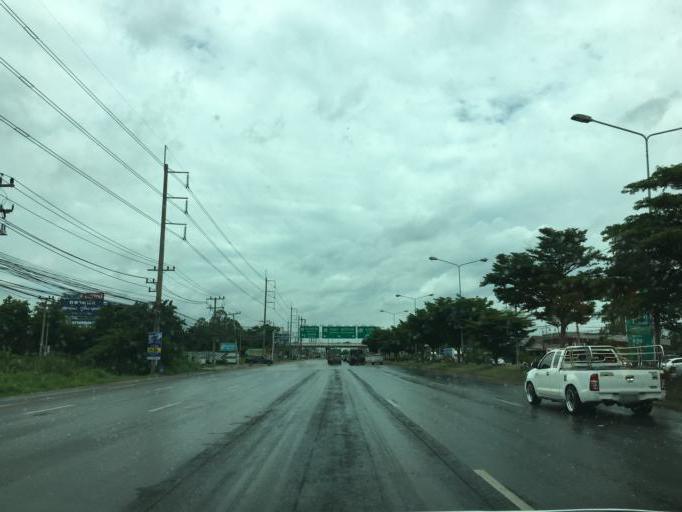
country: TH
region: Phra Nakhon Si Ayutthaya
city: Uthai
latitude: 14.3086
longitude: 100.6451
